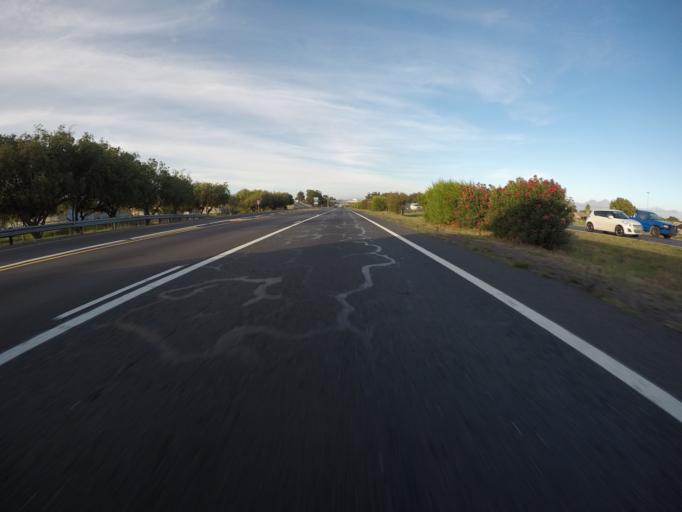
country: ZA
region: Western Cape
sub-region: City of Cape Town
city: Kraaifontein
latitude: -33.8469
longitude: 18.7124
